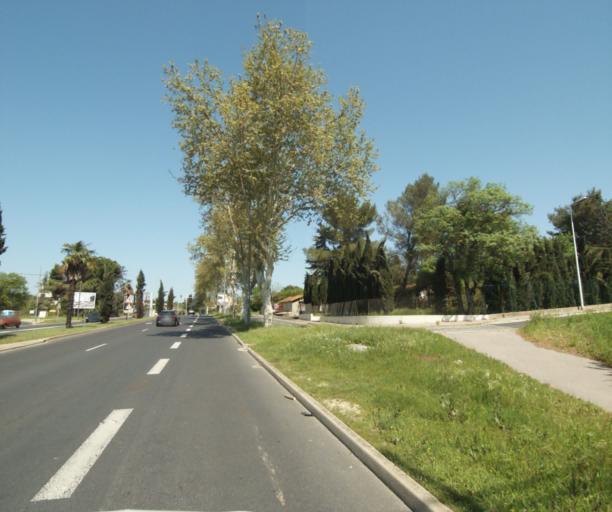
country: FR
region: Languedoc-Roussillon
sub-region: Departement de l'Herault
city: Montferrier-sur-Lez
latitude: 43.6417
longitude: 3.8464
